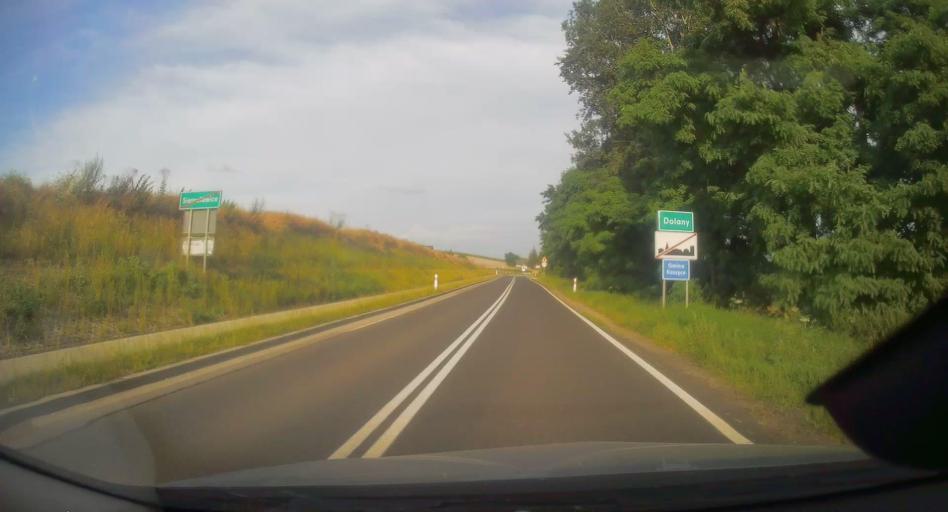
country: PL
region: Lesser Poland Voivodeship
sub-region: Powiat bochenski
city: Dziewin
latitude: 50.1433
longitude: 20.4770
